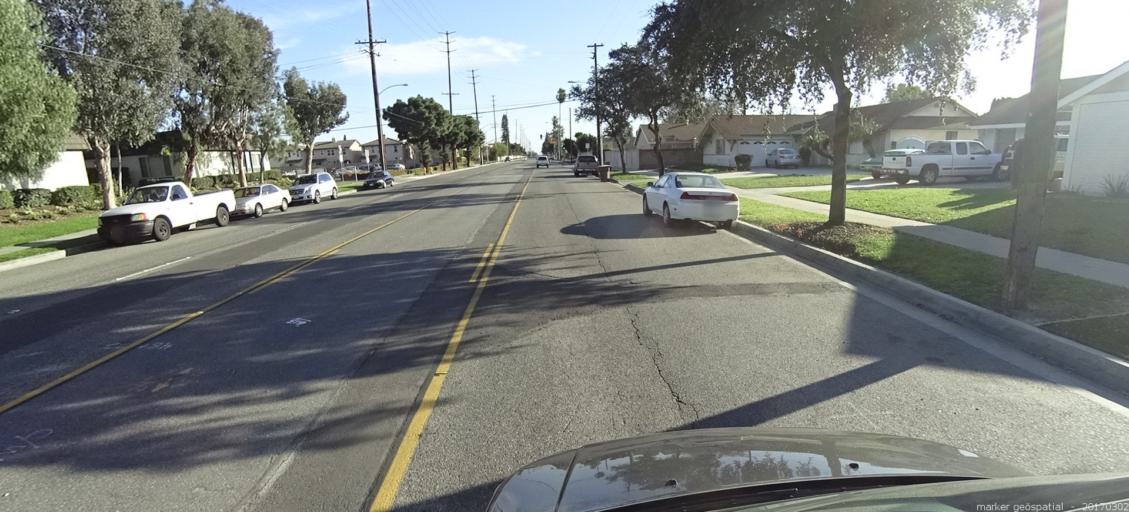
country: US
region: California
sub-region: Orange County
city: Placentia
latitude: 33.8449
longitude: -117.8717
